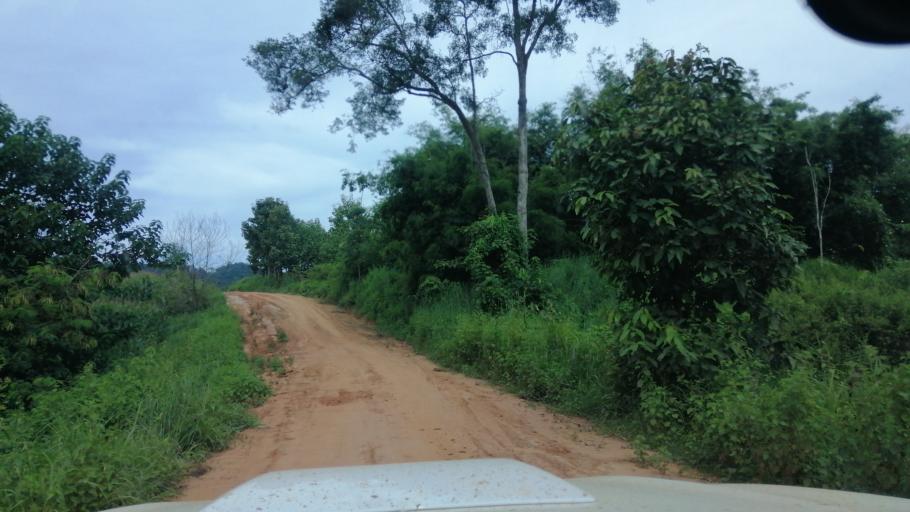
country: TH
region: Loei
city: Na Haeo
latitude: 17.5823
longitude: 101.1435
